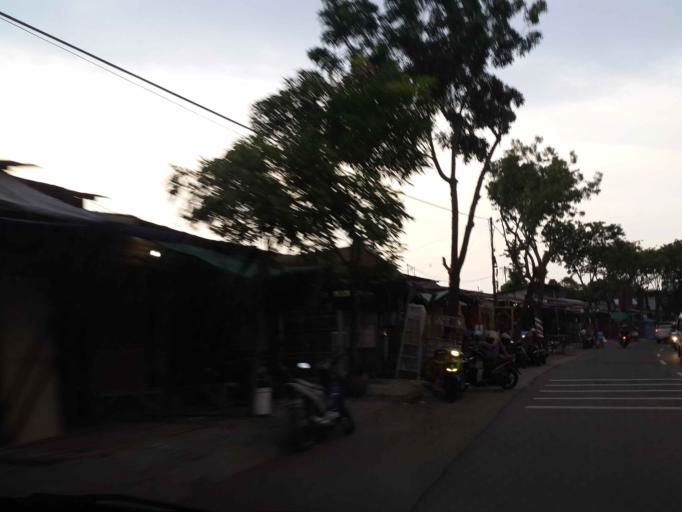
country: ID
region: East Java
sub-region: Kota Surabaya
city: Surabaya
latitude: -7.2515
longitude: 112.7292
